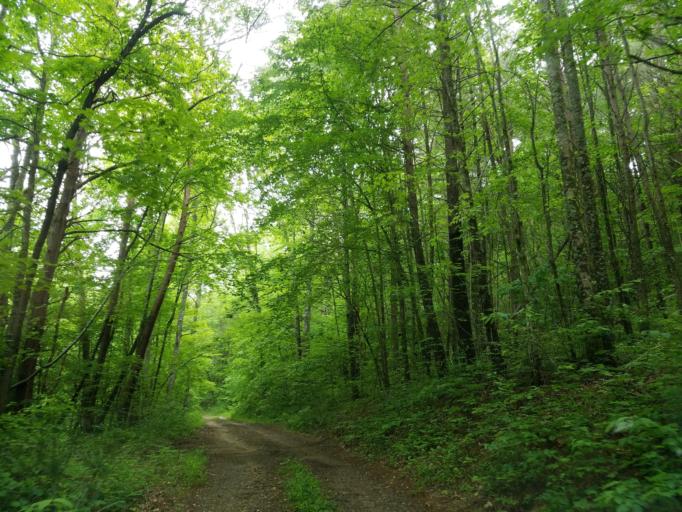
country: US
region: Georgia
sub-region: Union County
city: Blairsville
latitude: 34.7431
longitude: -84.0186
